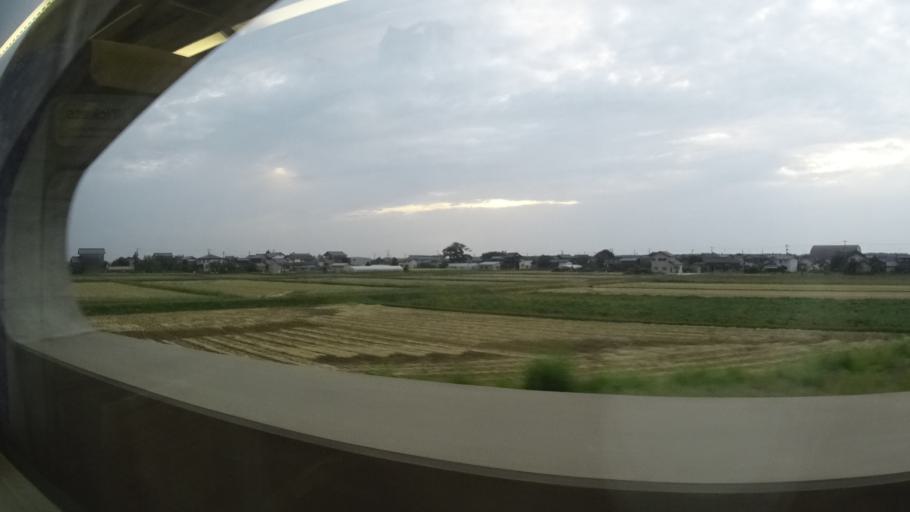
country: JP
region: Niigata
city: Murakami
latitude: 38.1751
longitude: 139.4594
